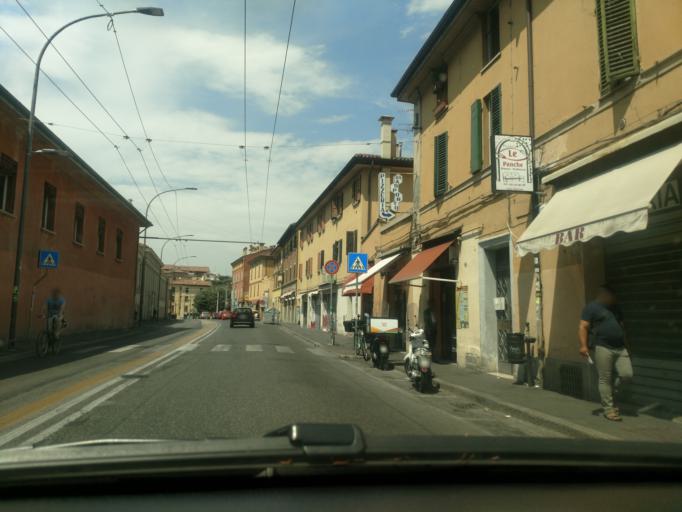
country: IT
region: Emilia-Romagna
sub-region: Provincia di Bologna
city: Bologna
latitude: 44.4937
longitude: 11.3589
